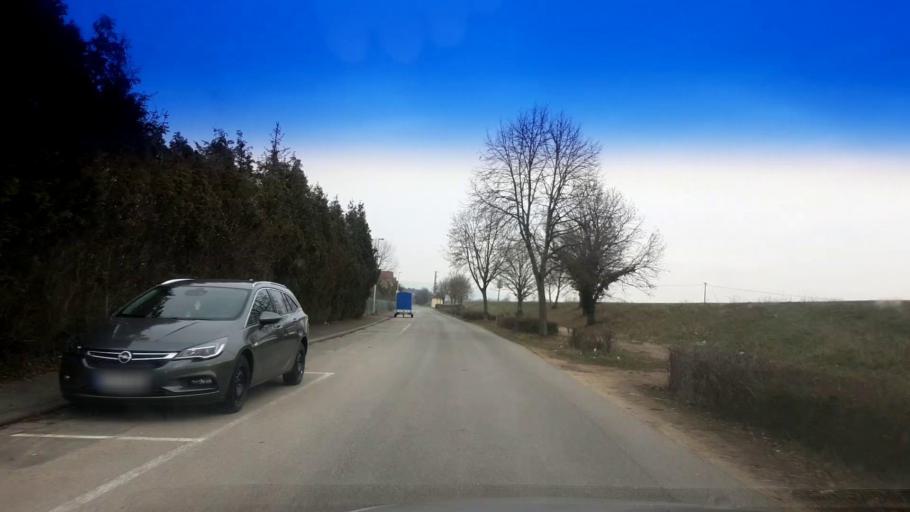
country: DE
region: Bavaria
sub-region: Upper Franconia
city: Hirschaid
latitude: 49.8128
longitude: 10.9889
